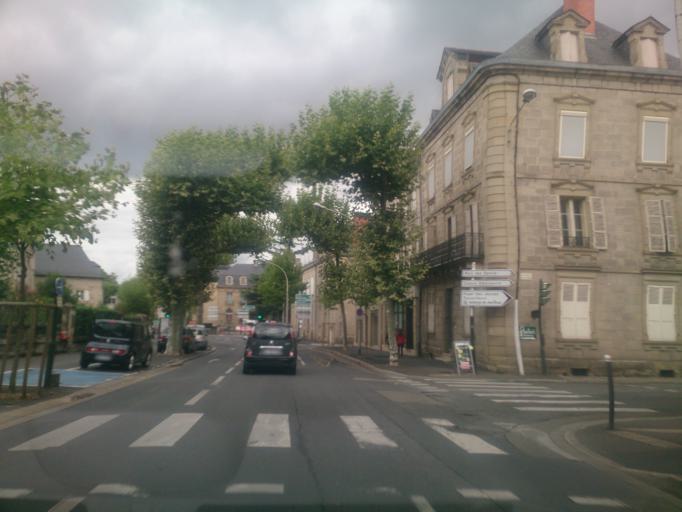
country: FR
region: Limousin
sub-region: Departement de la Correze
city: Brive-la-Gaillarde
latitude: 45.1598
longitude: 1.5355
